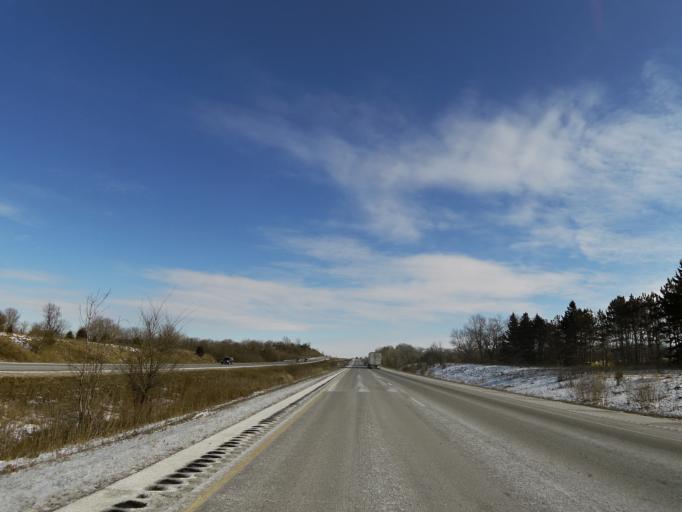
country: US
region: Wisconsin
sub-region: Saint Croix County
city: Roberts
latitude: 44.9634
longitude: -92.6471
